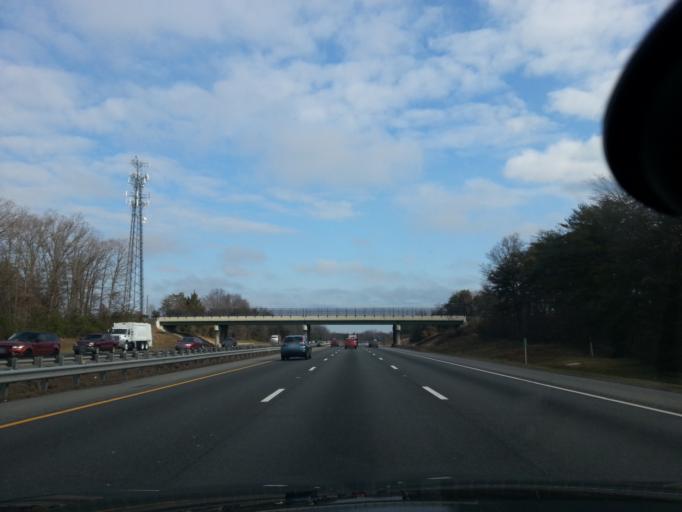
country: US
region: Virginia
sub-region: Spotsylvania County
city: Spotsylvania Courthouse
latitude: 38.1928
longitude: -77.5006
